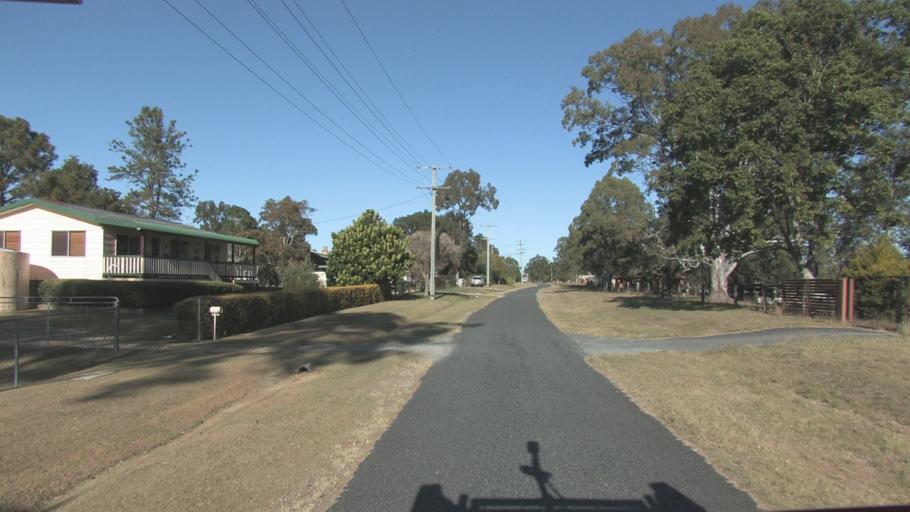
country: AU
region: Queensland
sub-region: Logan
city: Chambers Flat
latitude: -27.7594
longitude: 153.0529
